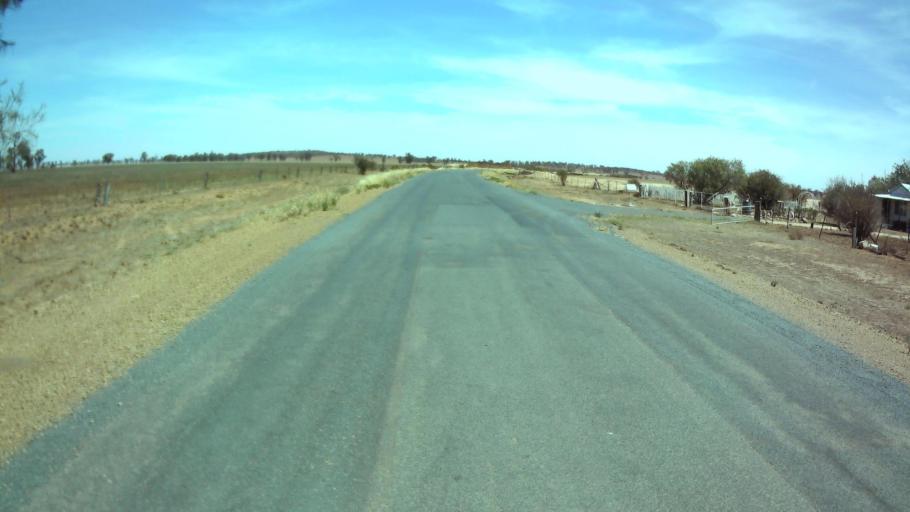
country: AU
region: New South Wales
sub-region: Weddin
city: Grenfell
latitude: -33.7500
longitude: 147.7670
